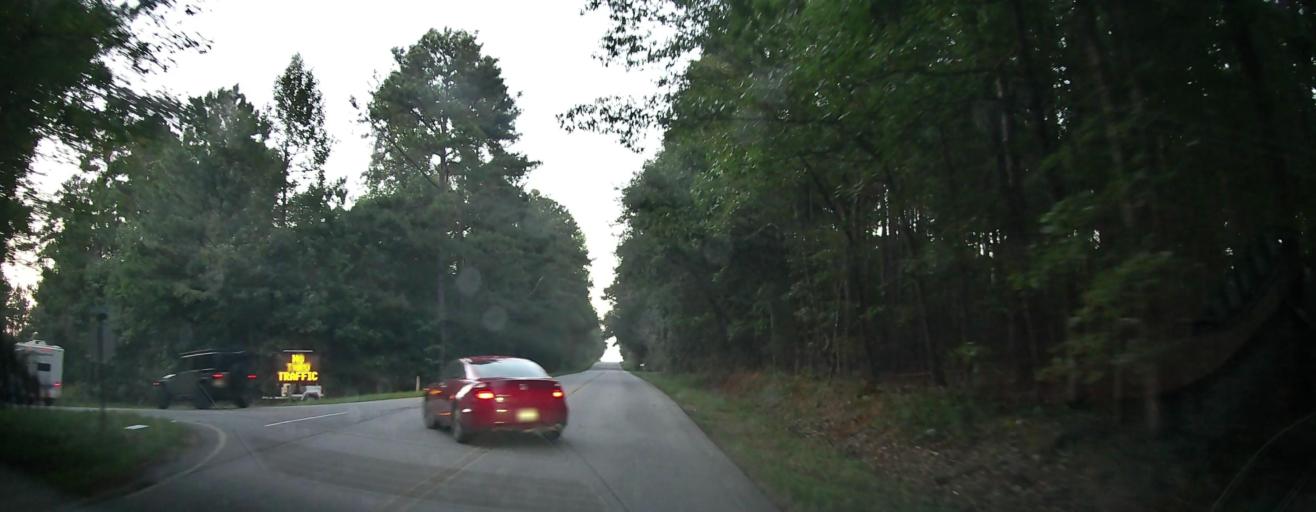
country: US
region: Georgia
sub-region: Butts County
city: Jackson
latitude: 33.2967
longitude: -84.0431
